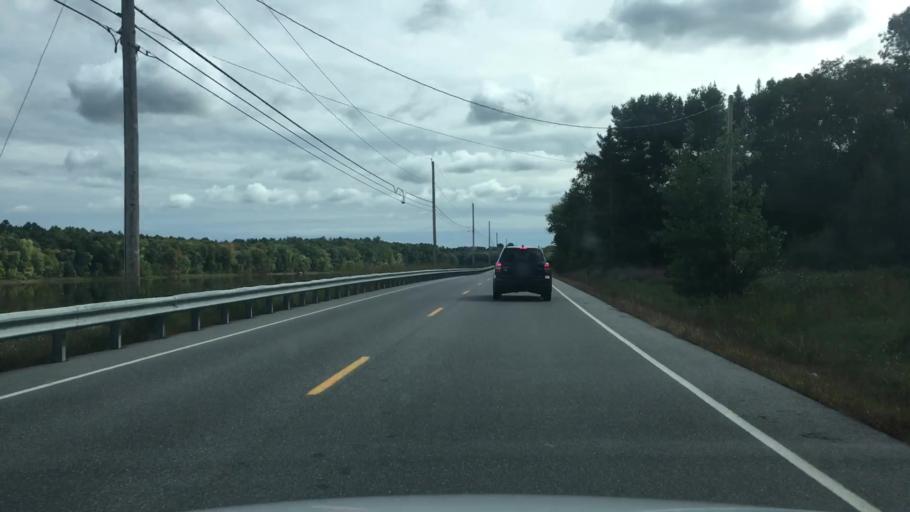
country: US
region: Maine
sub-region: Androscoggin County
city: Lisbon
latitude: 43.9951
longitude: -70.1435
